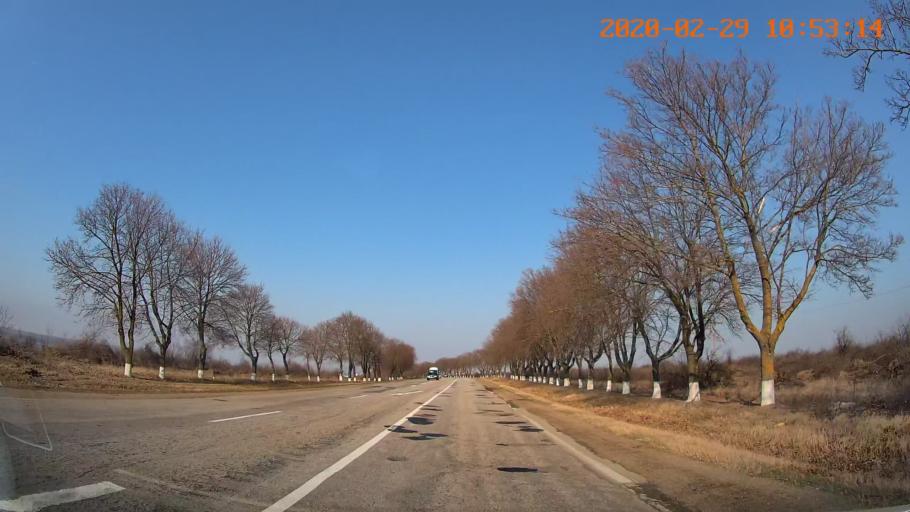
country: MD
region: Telenesti
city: Grigoriopol
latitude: 47.1138
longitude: 29.3390
